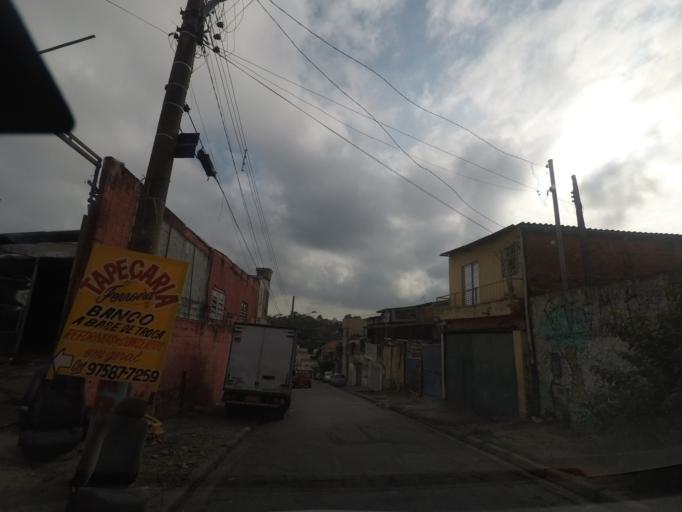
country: BR
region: Sao Paulo
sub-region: Osasco
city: Osasco
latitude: -23.5737
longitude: -46.7795
